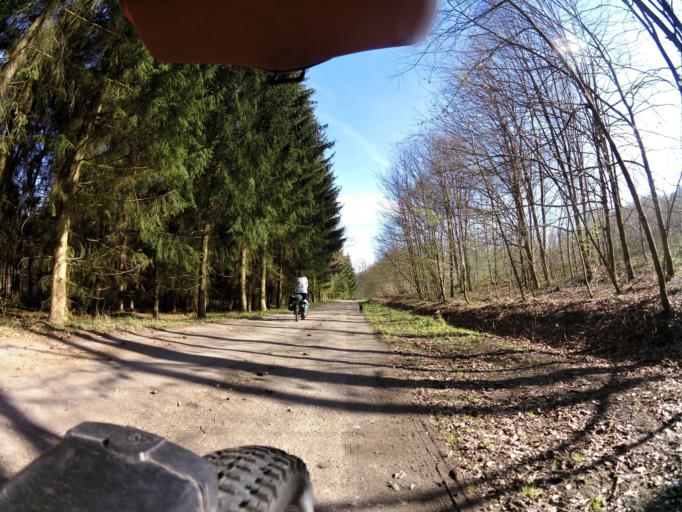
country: PL
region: West Pomeranian Voivodeship
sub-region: Powiat lobeski
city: Lobez
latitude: 53.7628
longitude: 15.5881
